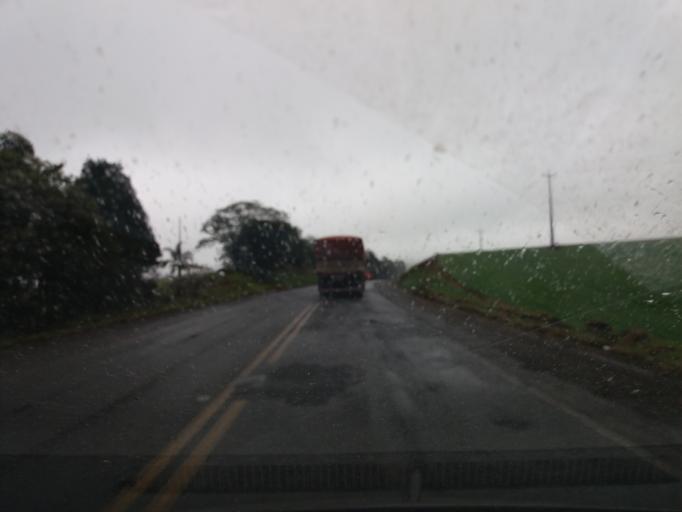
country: BR
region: Parana
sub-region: Francisco Beltrao
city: Francisco Beltrao
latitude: -26.0857
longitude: -53.2136
